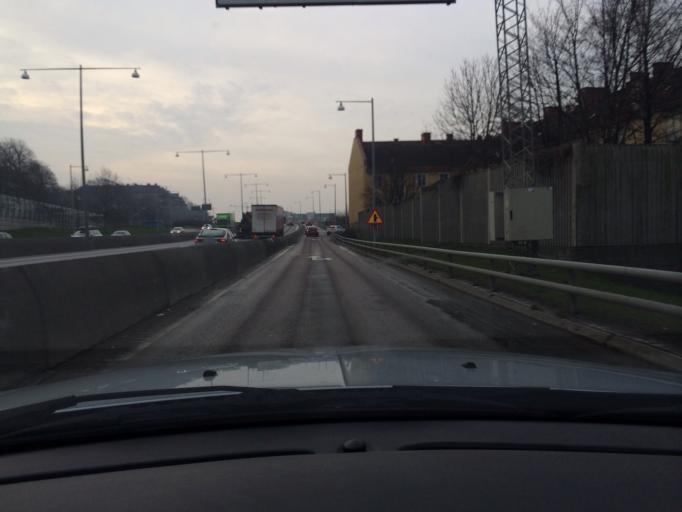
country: SE
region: Vaestra Goetaland
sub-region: Goteborg
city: Goeteborg
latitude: 57.7000
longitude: 11.9949
